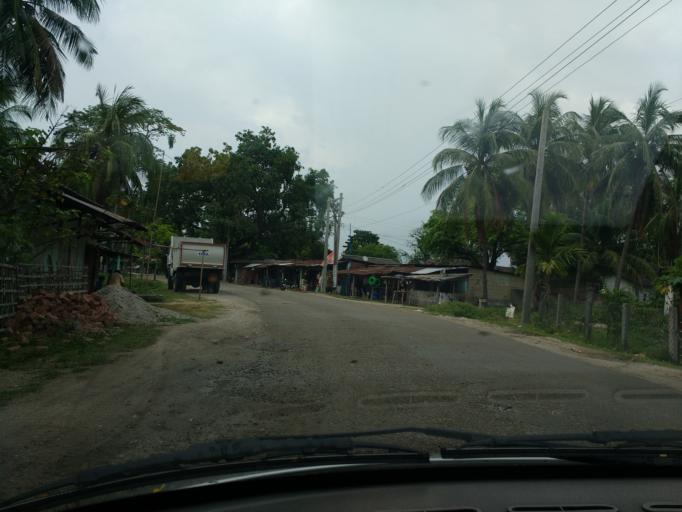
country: IN
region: Assam
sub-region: Udalguri
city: Udalguri
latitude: 26.7316
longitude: 92.2149
